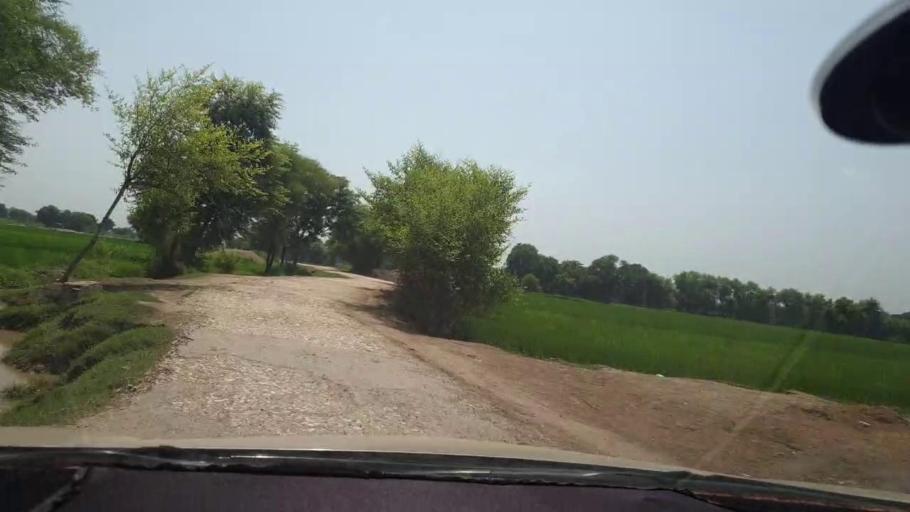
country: PK
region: Sindh
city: Kambar
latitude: 27.6688
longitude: 67.9433
